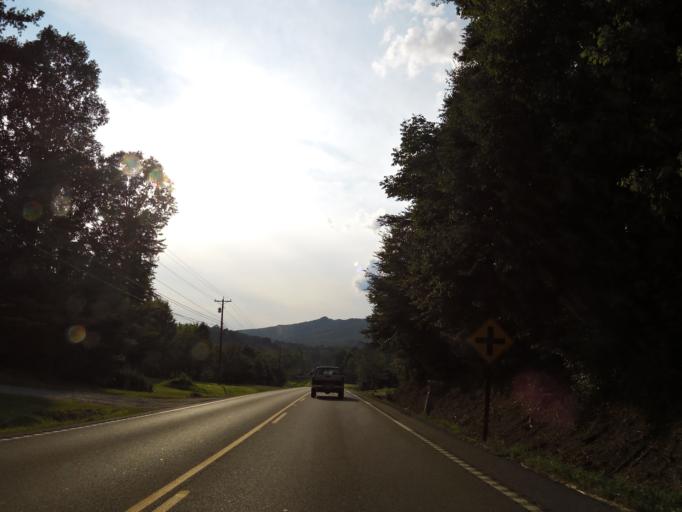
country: US
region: Tennessee
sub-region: Morgan County
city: Coalfield
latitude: 36.0361
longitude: -84.4251
